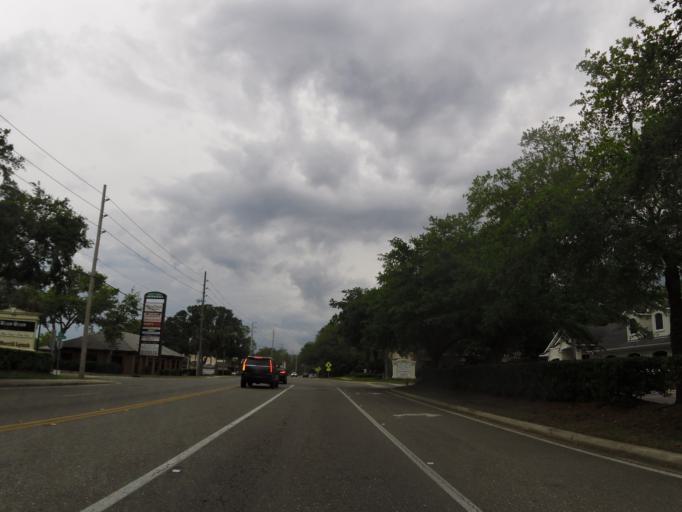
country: US
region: Florida
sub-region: Saint Johns County
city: Ponte Vedra Beach
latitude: 30.2274
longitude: -81.3864
